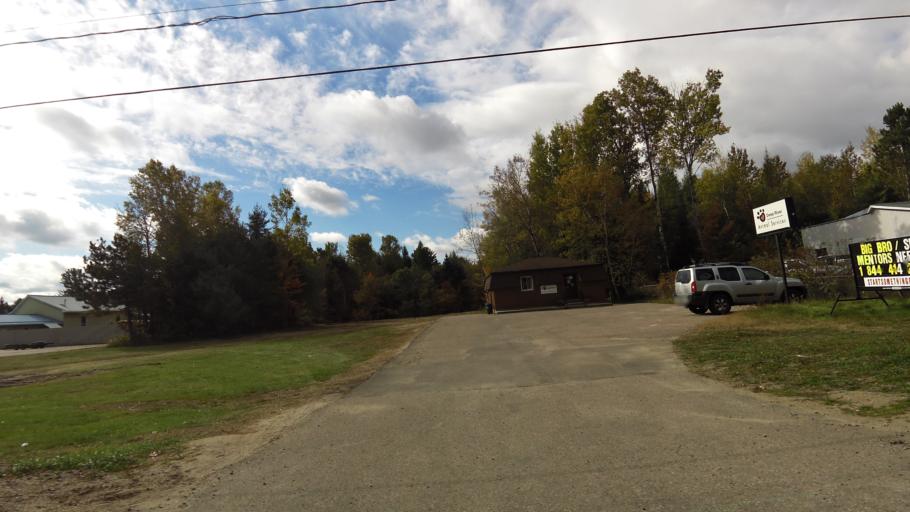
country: CA
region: Ontario
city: Deep River
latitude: 46.0986
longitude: -77.4960
